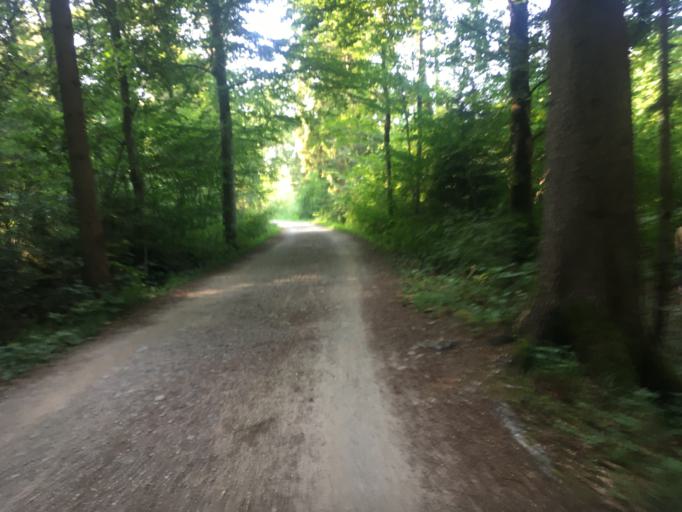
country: CH
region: Bern
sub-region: Emmental District
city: Oberburg
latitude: 47.0273
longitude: 7.6452
